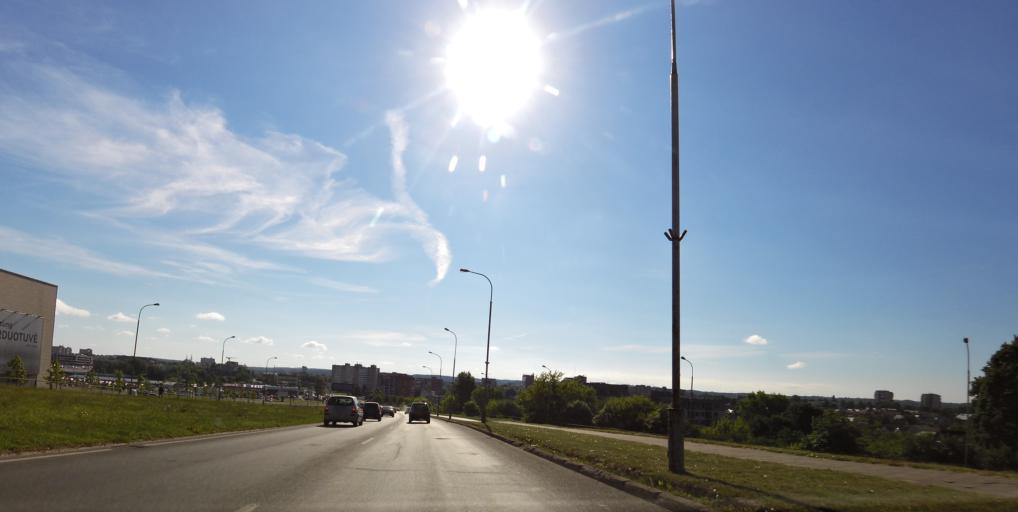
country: LT
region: Vilnius County
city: Seskine
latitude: 54.7127
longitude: 25.2718
